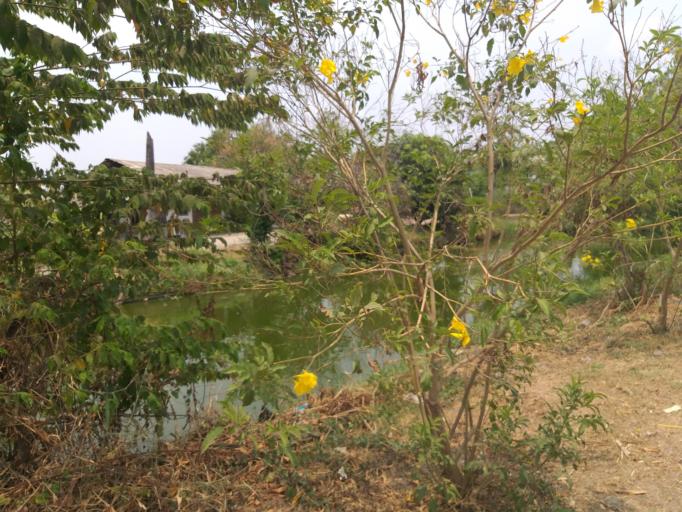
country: TH
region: Phra Nakhon Si Ayutthaya
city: Ban Bang Kadi Pathum Thani
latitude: 14.0084
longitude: 100.5717
